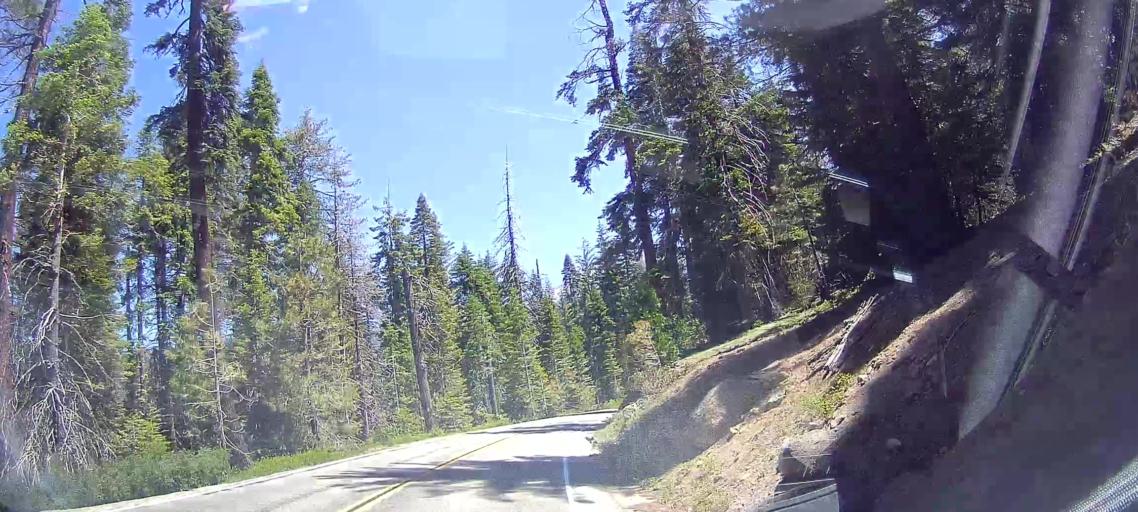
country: US
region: California
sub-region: Tulare County
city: Three Rivers
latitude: 36.5972
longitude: -118.7479
